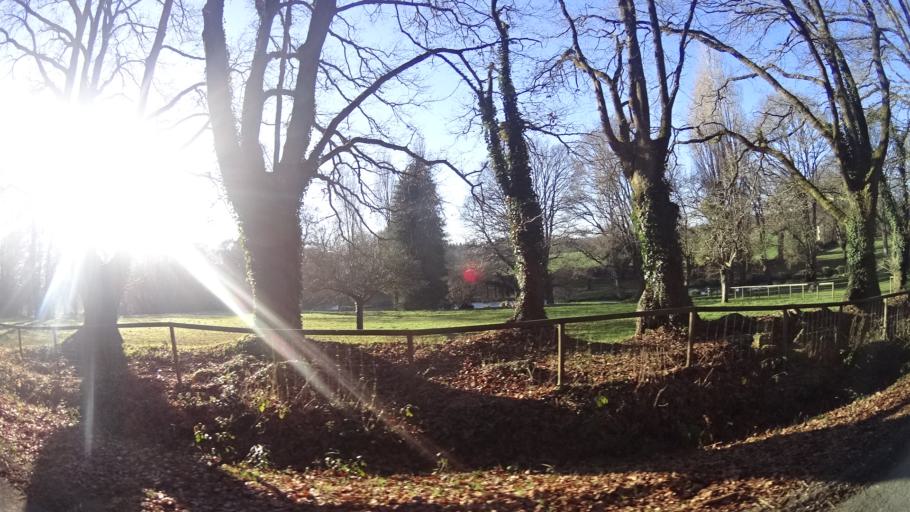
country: FR
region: Brittany
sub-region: Departement du Morbihan
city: Allaire
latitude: 47.6584
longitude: -2.1817
